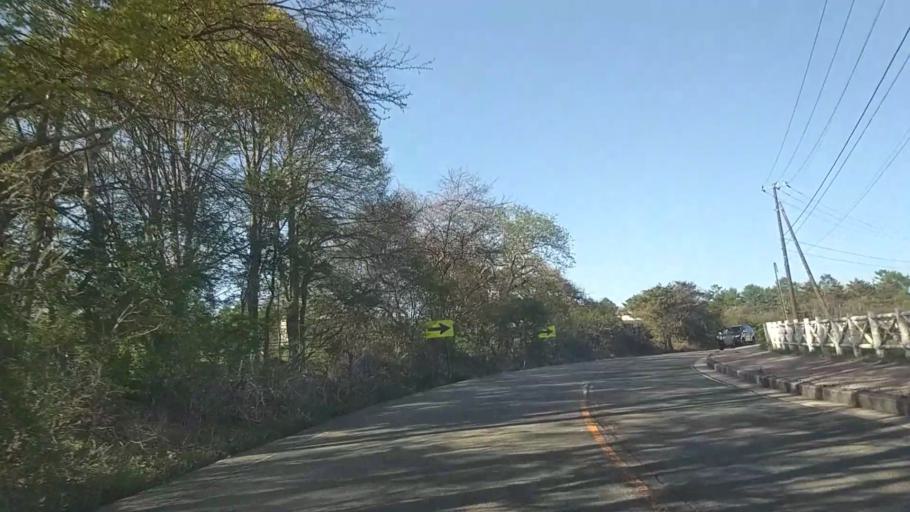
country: JP
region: Yamanashi
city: Nirasaki
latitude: 35.9292
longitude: 138.4084
